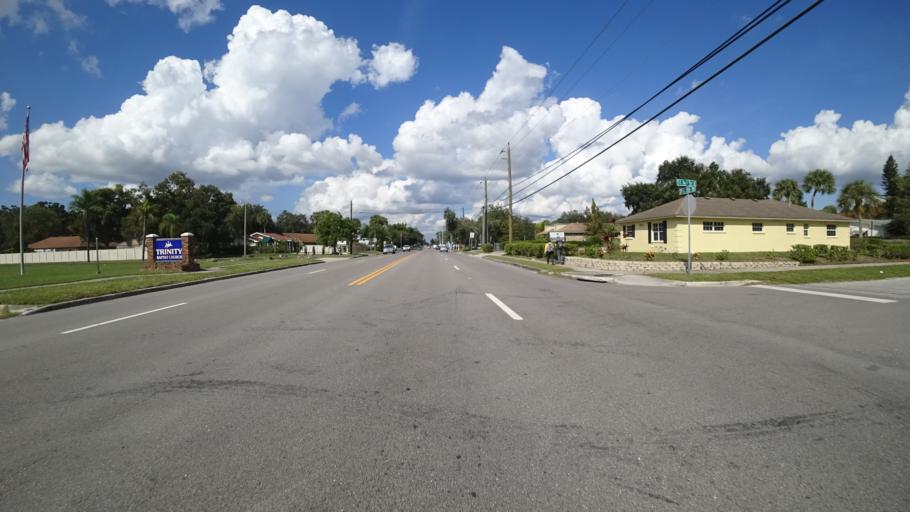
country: US
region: Florida
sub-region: Manatee County
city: South Bradenton
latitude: 27.4501
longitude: -82.5876
